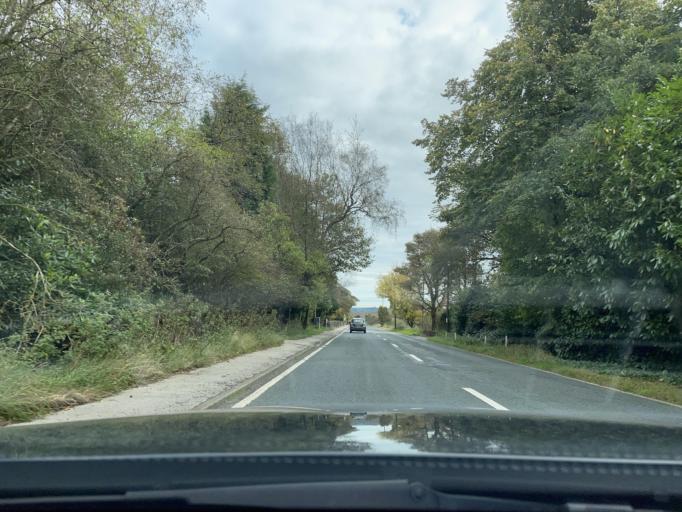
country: GB
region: England
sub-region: Sheffield
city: Bradfield
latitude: 53.3890
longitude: -1.6368
